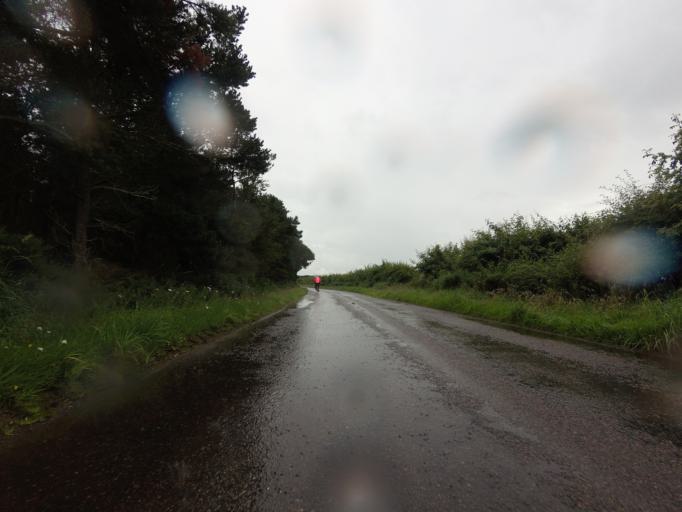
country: GB
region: Scotland
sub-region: Moray
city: Fochabers
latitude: 57.6664
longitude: -3.0767
